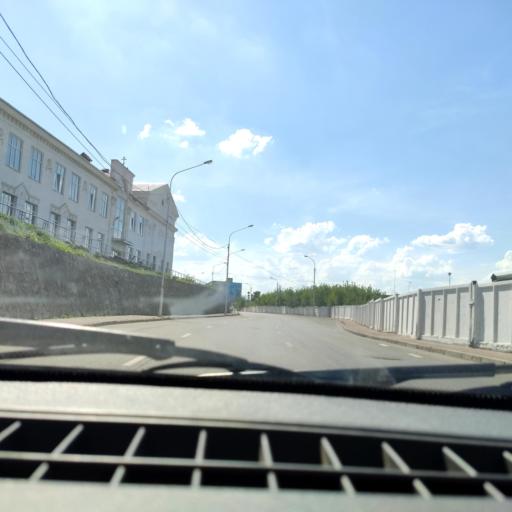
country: RU
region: Bashkortostan
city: Ufa
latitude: 54.7478
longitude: 55.9472
